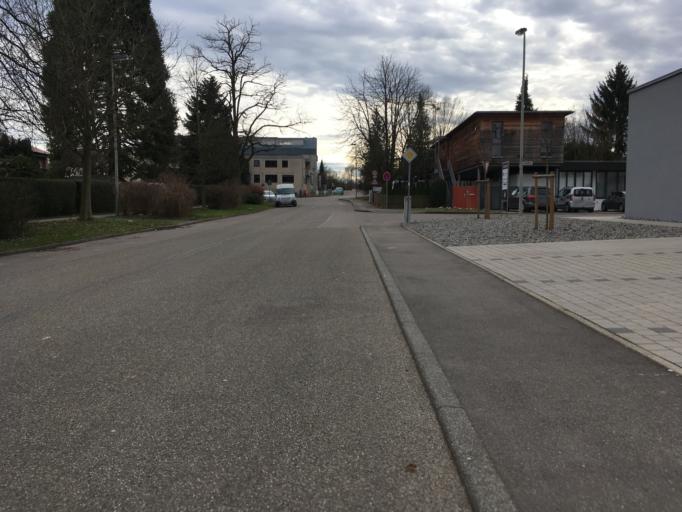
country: DE
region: Baden-Wuerttemberg
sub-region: Regierungsbezirk Stuttgart
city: Freiberg am Neckar
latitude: 48.9338
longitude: 9.1793
